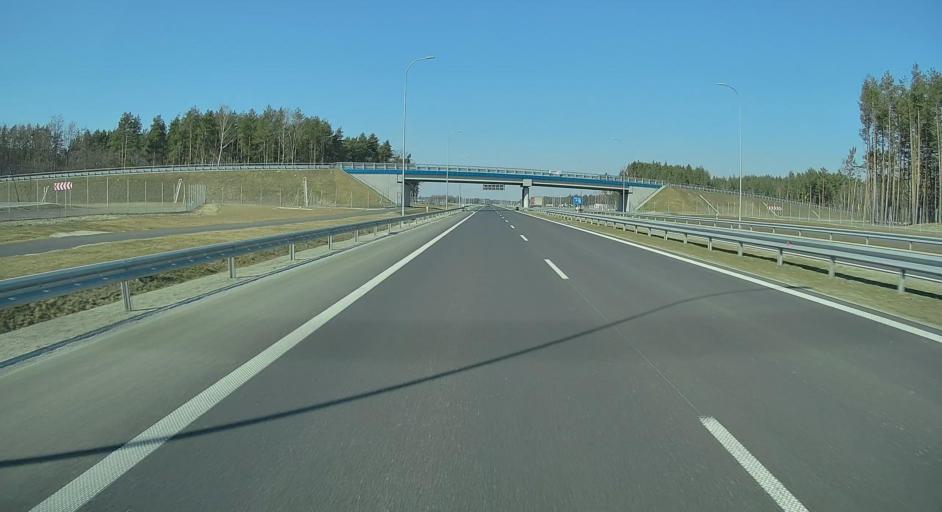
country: PL
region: Subcarpathian Voivodeship
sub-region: Powiat nizanski
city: Jezowe
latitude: 50.3834
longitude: 22.1649
